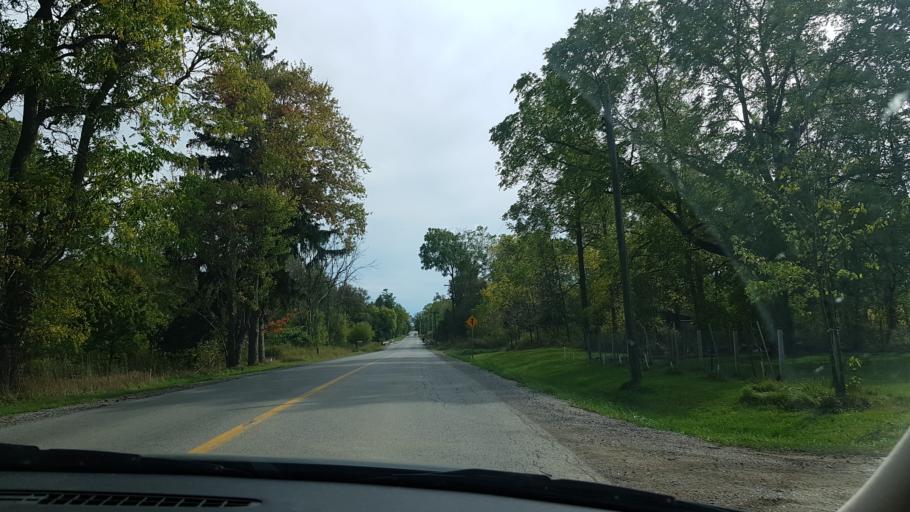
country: CA
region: Ontario
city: Delaware
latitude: 43.0082
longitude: -81.4001
